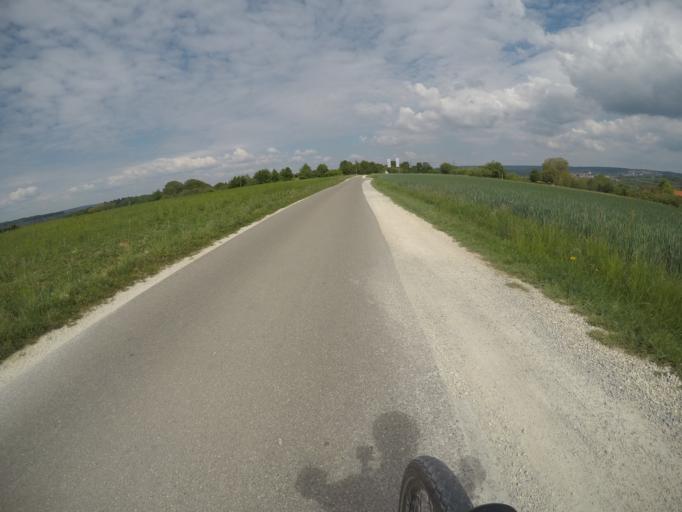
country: DE
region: Baden-Wuerttemberg
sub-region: Regierungsbezirk Stuttgart
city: Notzingen
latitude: 48.6681
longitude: 9.4302
